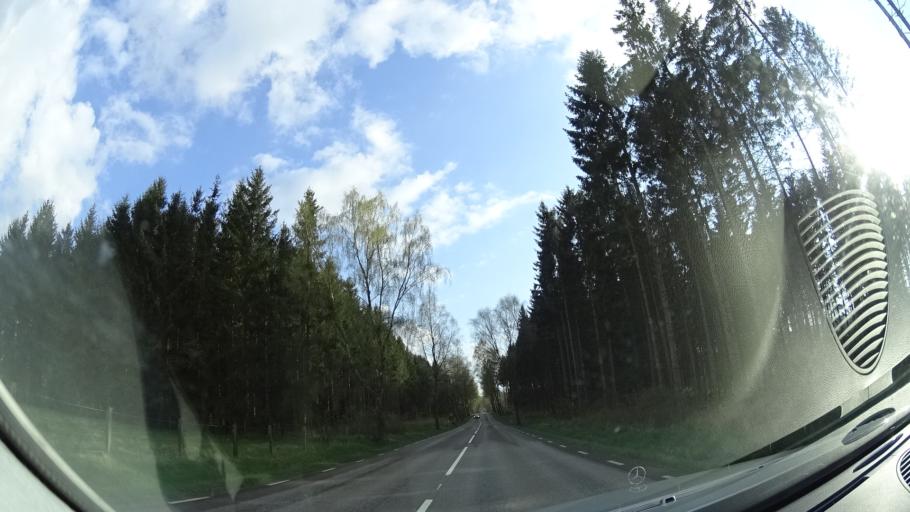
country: SE
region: Skane
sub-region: Klippans Kommun
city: Ljungbyhed
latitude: 56.0598
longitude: 13.2456
